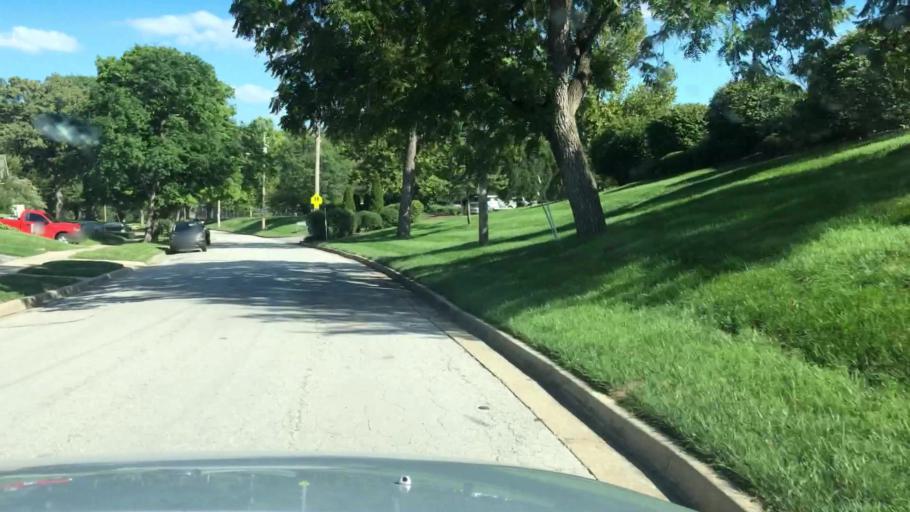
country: US
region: Kansas
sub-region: Johnson County
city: Westwood
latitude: 39.0356
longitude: -94.6056
